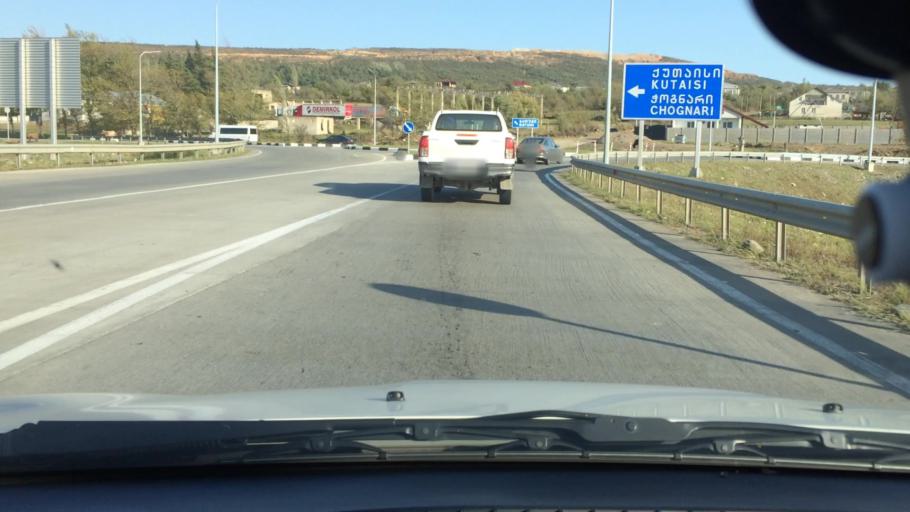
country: GE
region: Imereti
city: Kutaisi
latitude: 42.2128
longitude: 42.8193
